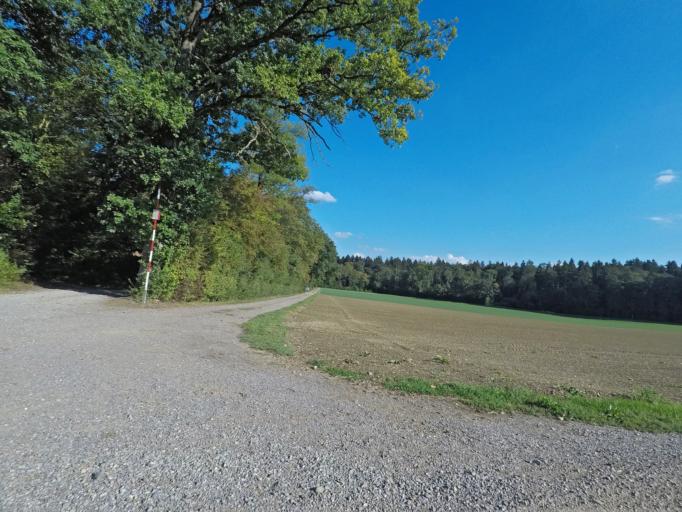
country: CH
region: Thurgau
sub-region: Frauenfeld District
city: Diessenhofen
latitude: 47.6579
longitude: 8.7376
